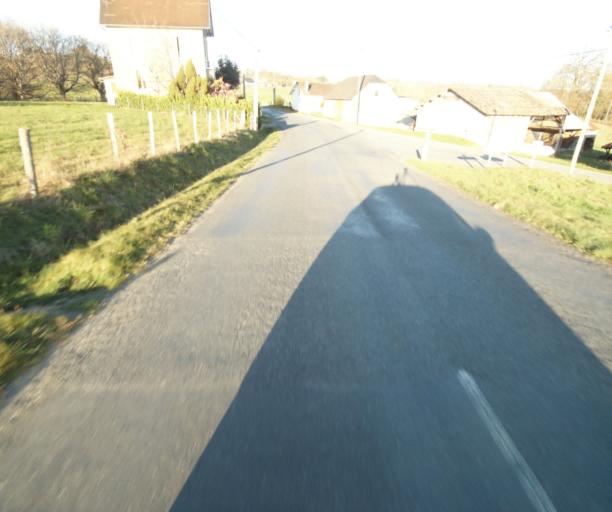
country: FR
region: Limousin
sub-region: Departement de la Correze
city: Saint-Mexant
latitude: 45.3285
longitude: 1.6025
